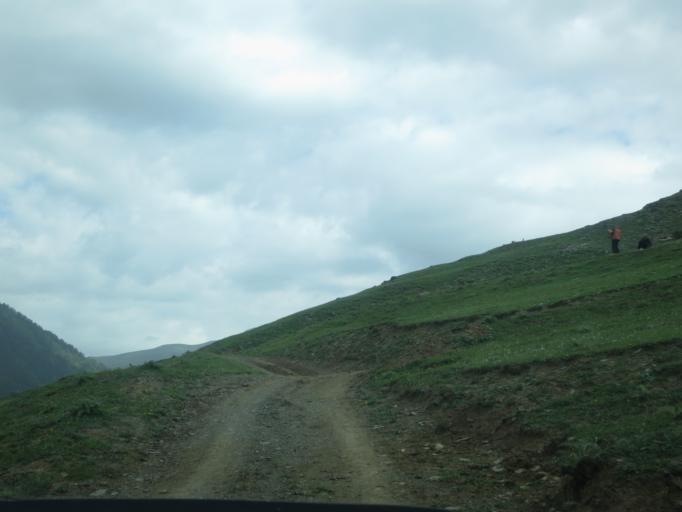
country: RU
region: Chechnya
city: Itum-Kali
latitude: 42.3739
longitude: 45.6330
